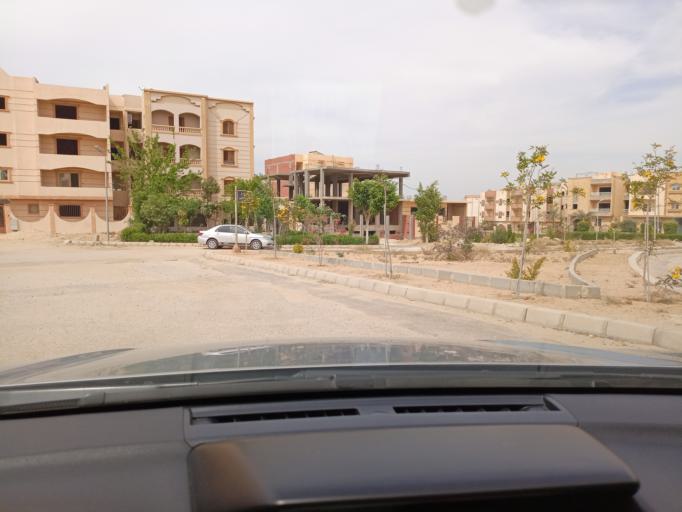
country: EG
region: Muhafazat al Qalyubiyah
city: Al Khankah
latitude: 30.2440
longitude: 31.4927
